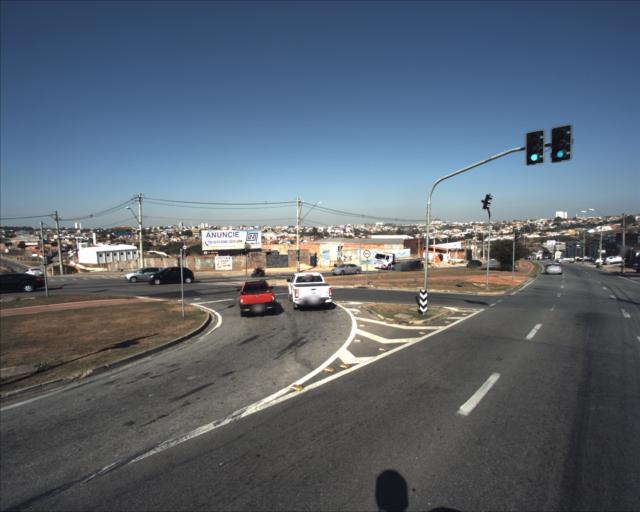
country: BR
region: Sao Paulo
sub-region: Sorocaba
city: Sorocaba
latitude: -23.4864
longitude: -47.4908
